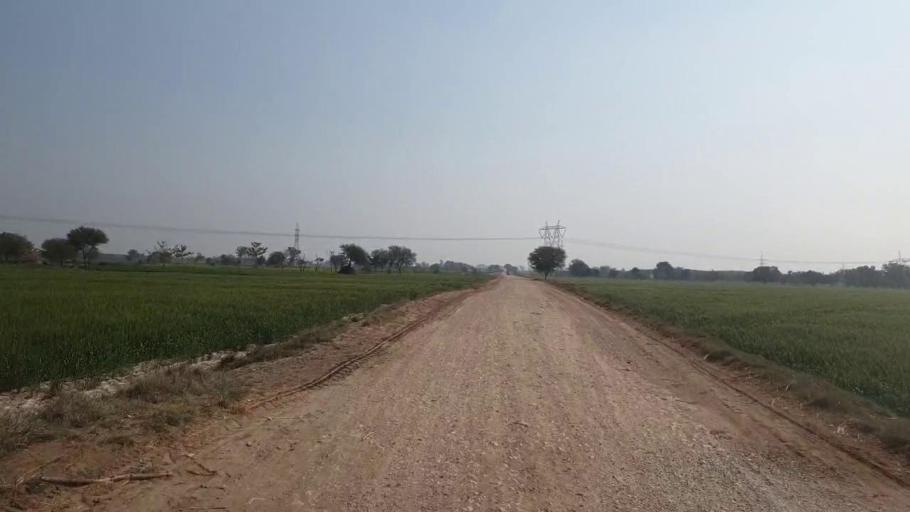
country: PK
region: Sindh
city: Bhit Shah
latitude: 25.7244
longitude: 68.5372
